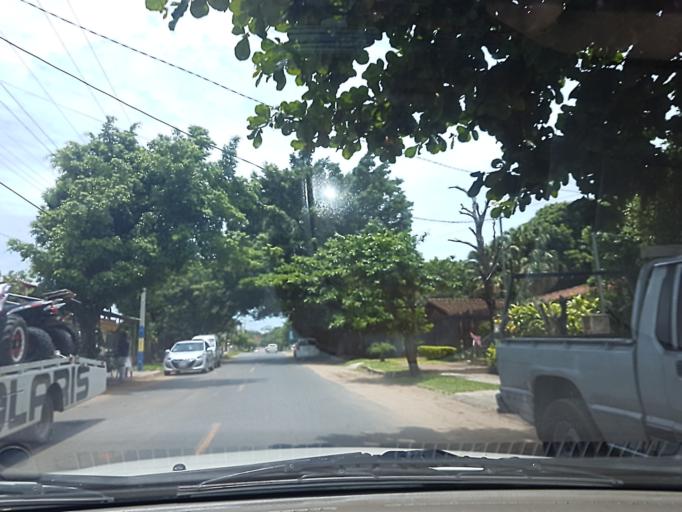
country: PY
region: Central
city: Fernando de la Mora
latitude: -25.2538
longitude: -57.5107
